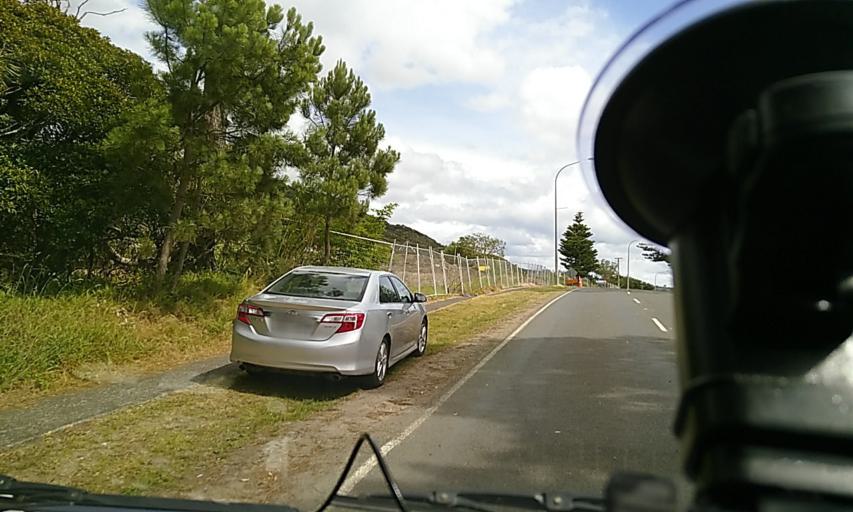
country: NZ
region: Northland
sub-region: Far North District
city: Ahipara
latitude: -35.5063
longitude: 173.3904
